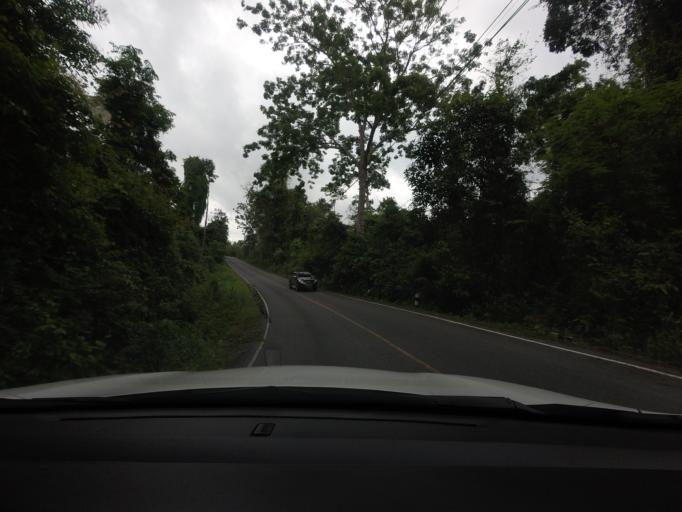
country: TH
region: Nakhon Ratchasima
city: Pak Chong
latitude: 14.4753
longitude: 101.3848
